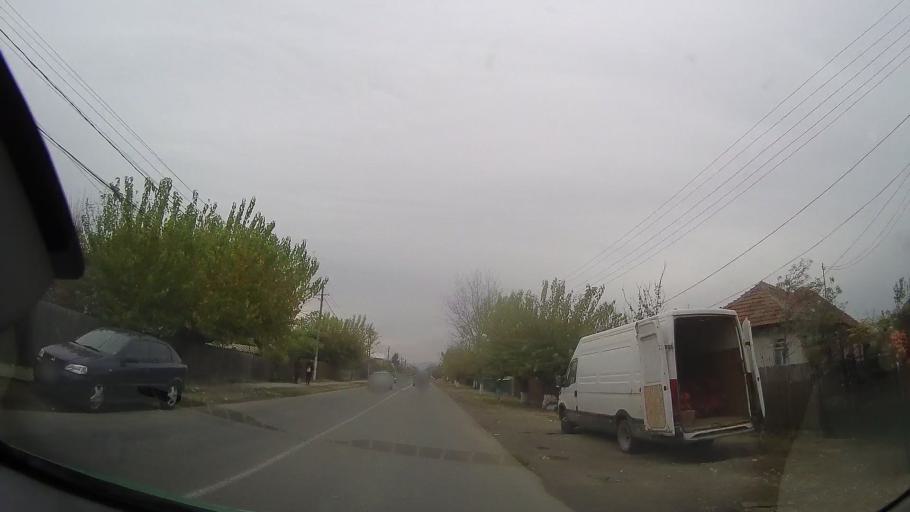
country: RO
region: Prahova
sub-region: Comuna Albesti-Paleologu
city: Albesti-Paleologu
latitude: 44.9550
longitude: 26.2301
